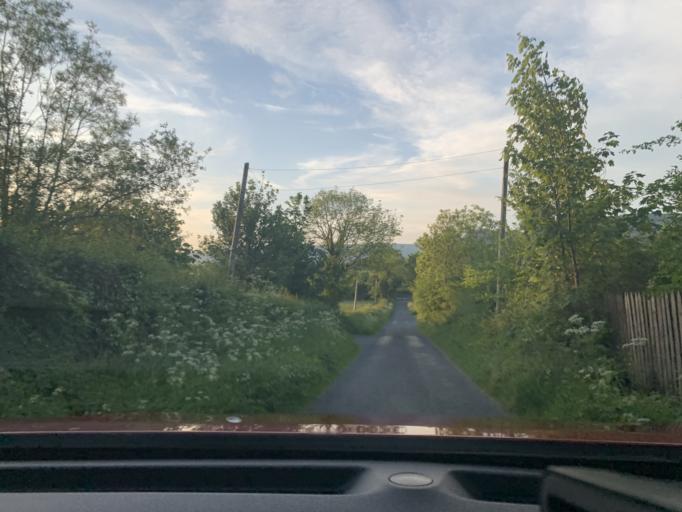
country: IE
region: Connaught
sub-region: Sligo
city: Sligo
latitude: 54.2892
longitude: -8.4307
